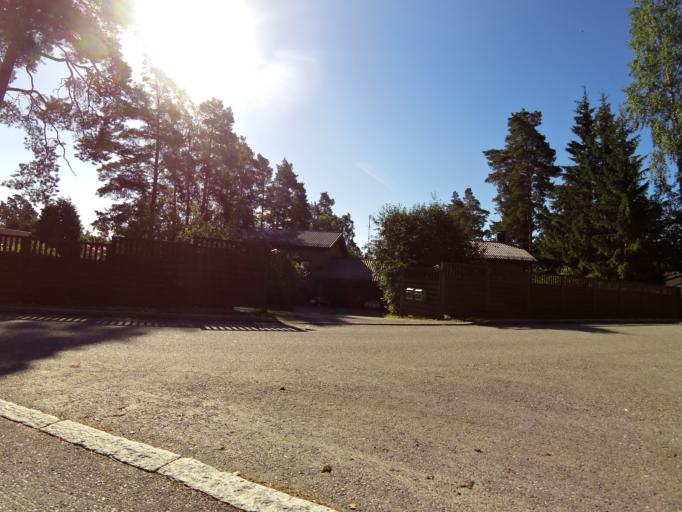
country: FI
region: Uusimaa
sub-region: Helsinki
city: Espoo
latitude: 60.1580
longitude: 24.6650
